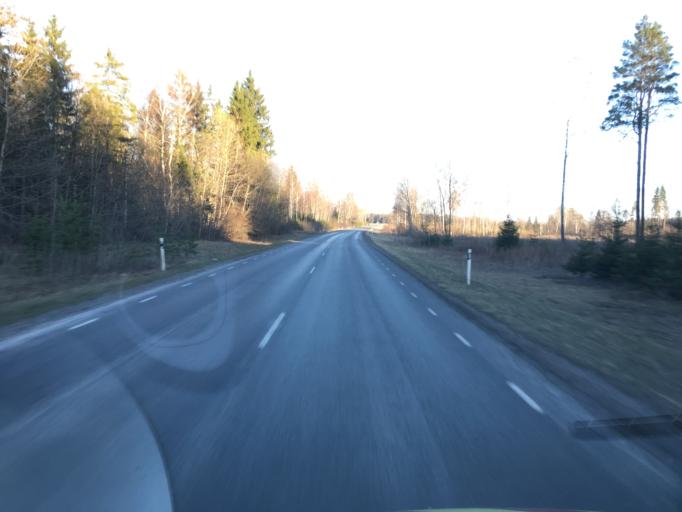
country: EE
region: Raplamaa
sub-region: Kehtna vald
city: Kehtna
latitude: 59.0627
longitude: 24.9331
